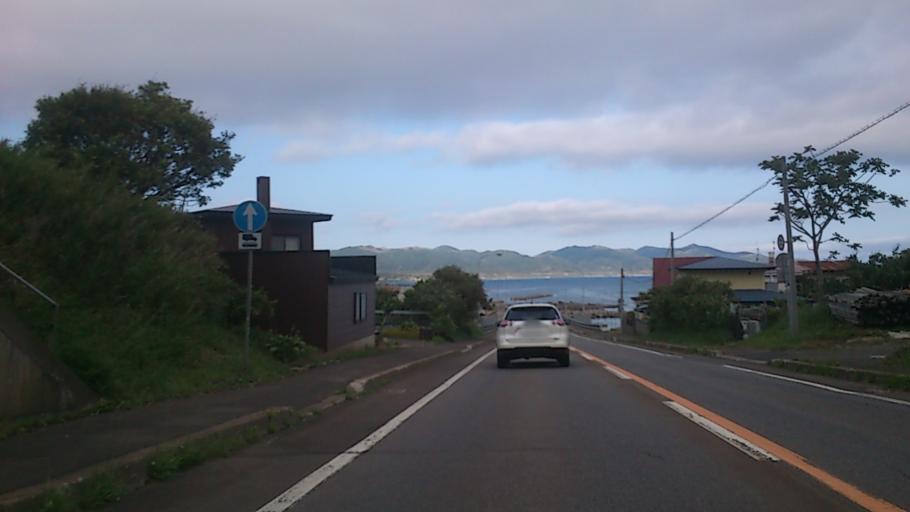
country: JP
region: Aomori
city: Shimokizukuri
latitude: 41.4247
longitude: 140.0903
